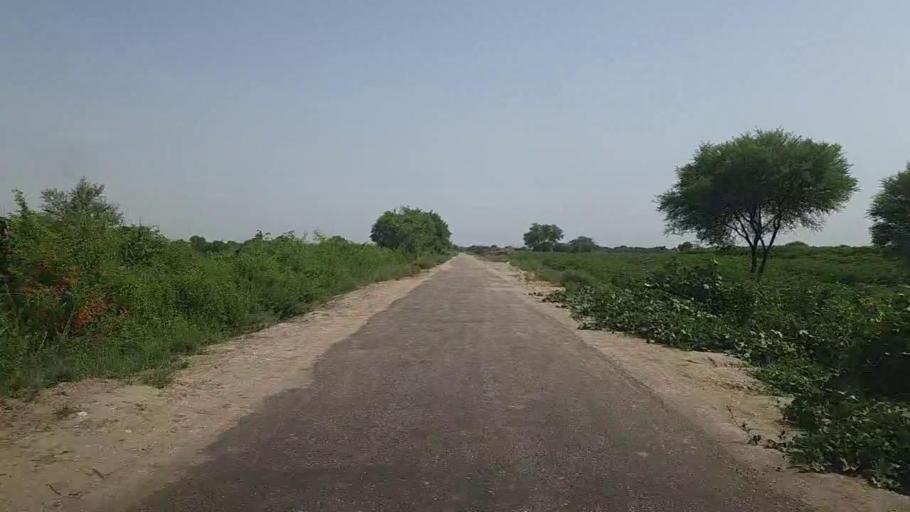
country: PK
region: Sindh
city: Pad Idan
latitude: 26.8363
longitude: 68.3307
